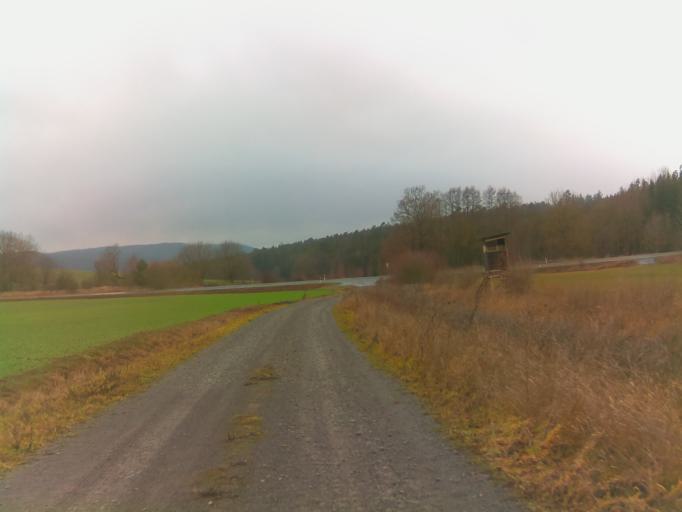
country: DE
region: Thuringia
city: Juchsen
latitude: 50.4602
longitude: 10.4719
